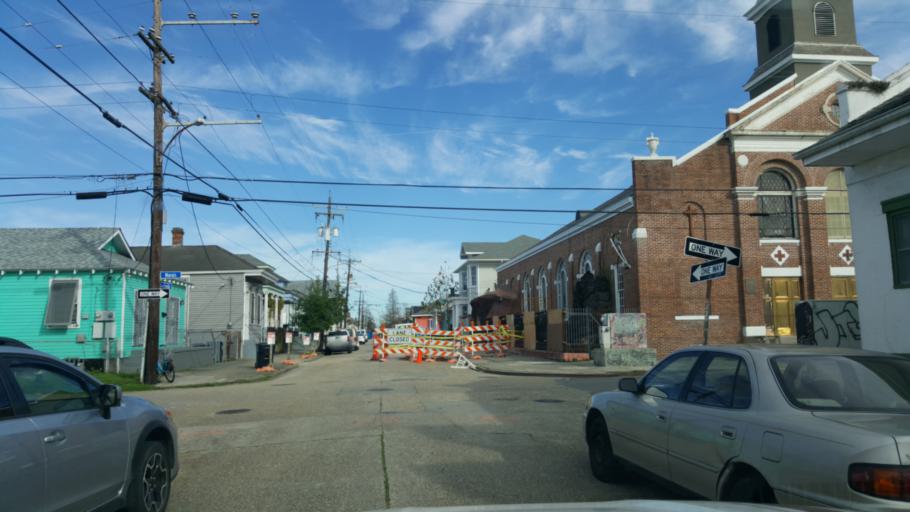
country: US
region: Louisiana
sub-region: Orleans Parish
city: New Orleans
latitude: 29.9695
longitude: -90.0545
